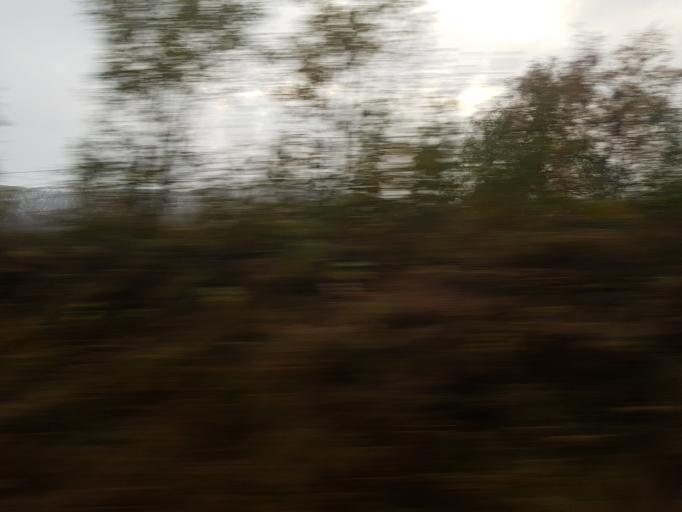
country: NO
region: Oppland
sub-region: Dovre
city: Dombas
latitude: 62.0274
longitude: 9.1815
